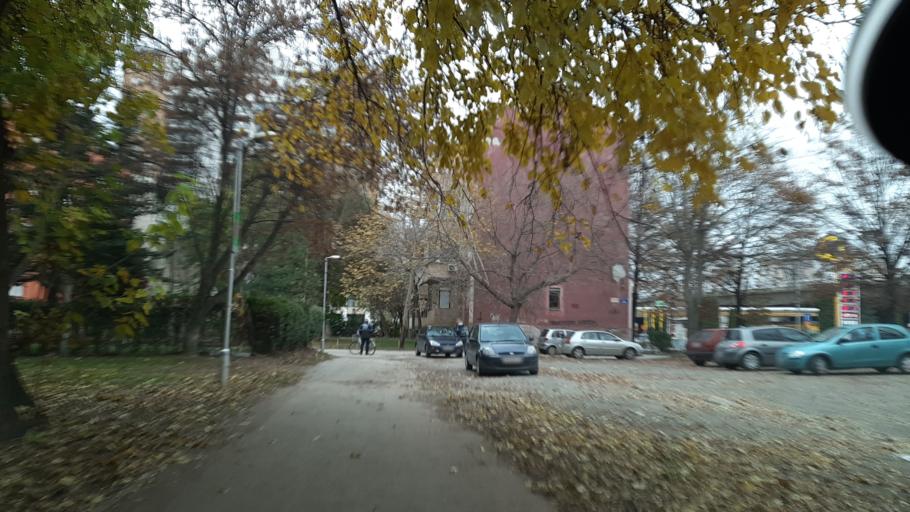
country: MK
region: Karpos
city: Skopje
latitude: 41.9896
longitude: 21.4427
